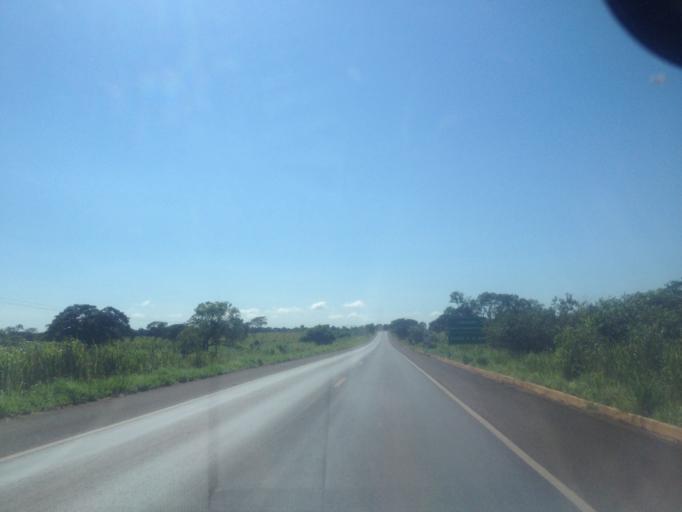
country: BR
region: Minas Gerais
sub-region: Santa Vitoria
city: Santa Vitoria
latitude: -18.9835
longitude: -50.5845
